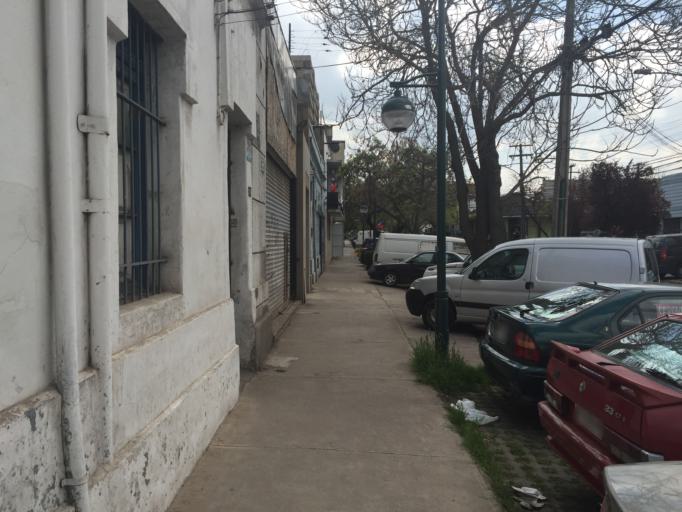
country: CL
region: Santiago Metropolitan
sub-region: Provincia de Santiago
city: Santiago
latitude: -33.4491
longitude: -70.6252
